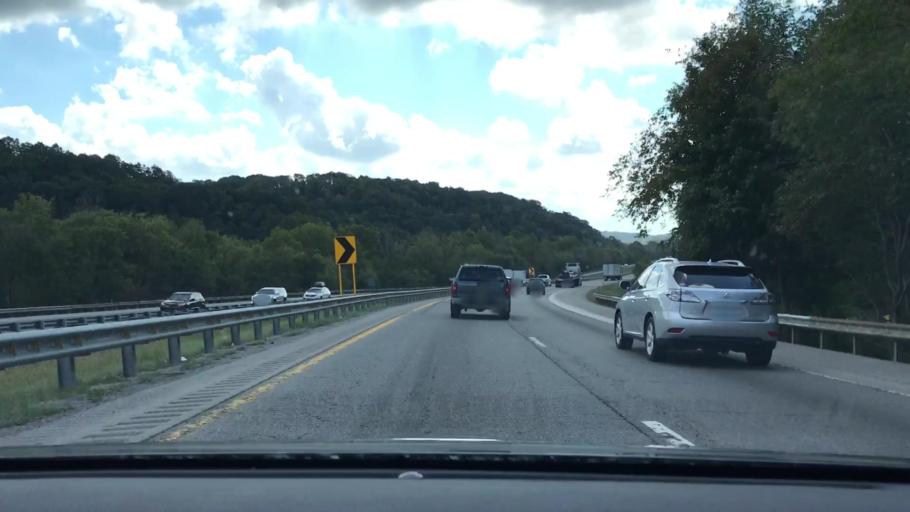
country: US
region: Tennessee
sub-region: Sumner County
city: Millersville
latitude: 36.3988
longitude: -86.7177
